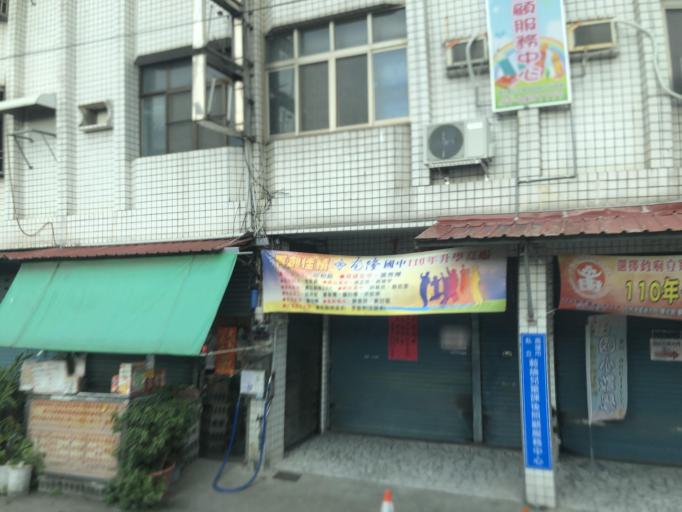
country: TW
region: Taiwan
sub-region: Pingtung
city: Pingtung
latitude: 22.8672
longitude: 120.5365
